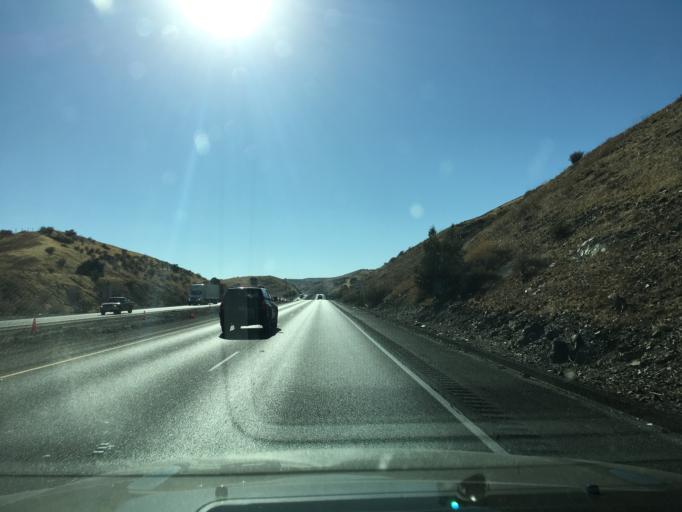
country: US
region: California
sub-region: Merced County
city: Gustine
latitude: 37.1010
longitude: -121.1415
